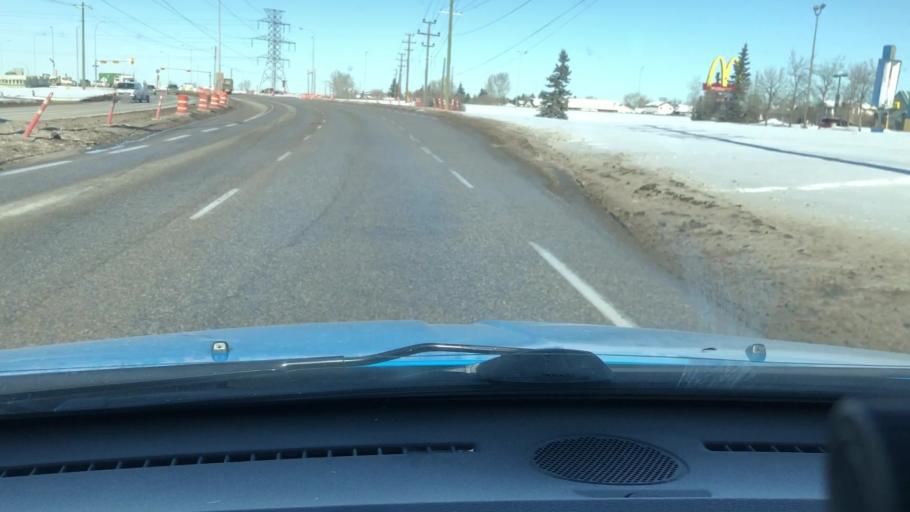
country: CA
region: Alberta
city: Calgary
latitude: 51.0130
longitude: -114.0017
